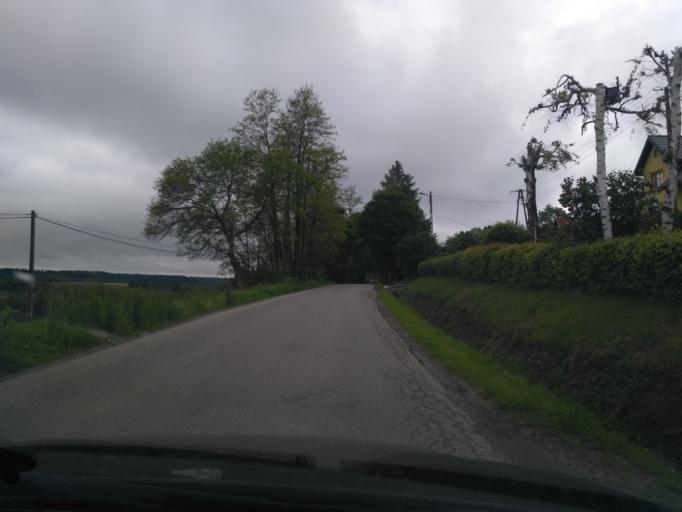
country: PL
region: Subcarpathian Voivodeship
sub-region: Powiat strzyzowski
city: Frysztak
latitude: 49.8051
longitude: 21.5772
